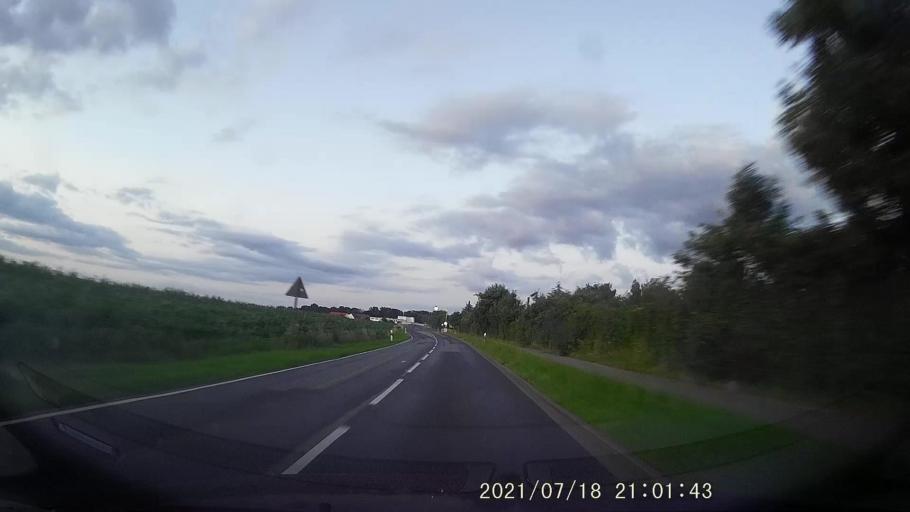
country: DE
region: Saxony
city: Goerlitz
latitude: 51.1623
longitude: 14.9529
